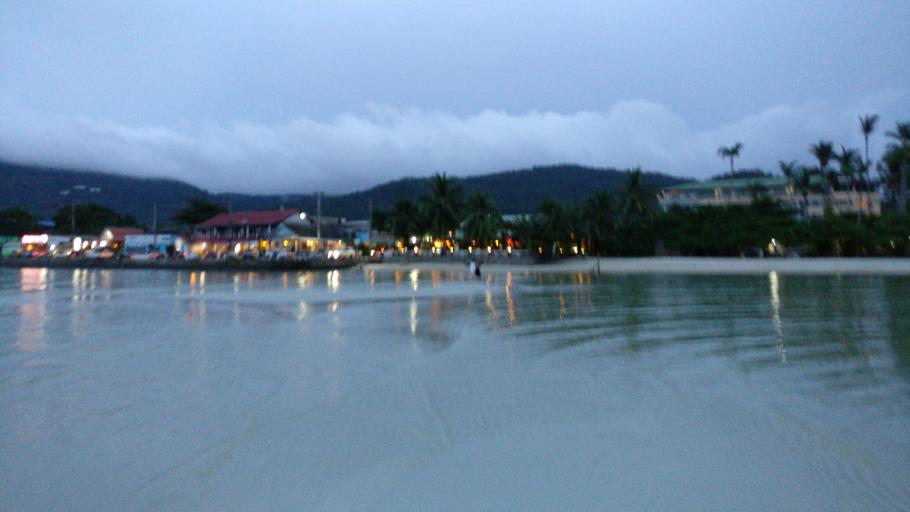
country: TH
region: Surat Thani
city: Ko Samui
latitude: 9.5299
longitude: 99.9335
